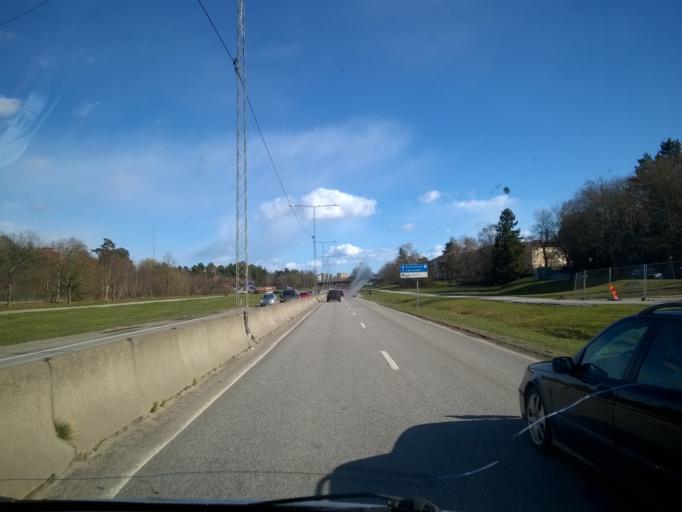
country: SE
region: Stockholm
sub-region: Jarfalla Kommun
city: Jakobsberg
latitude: 59.3703
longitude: 17.8497
